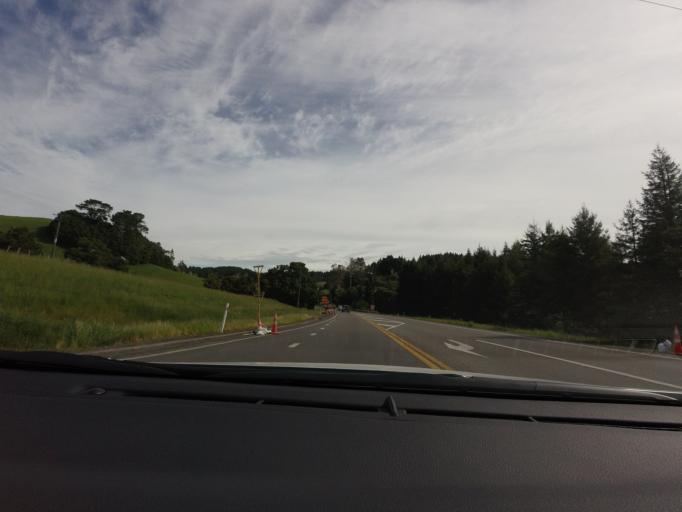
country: NZ
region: Auckland
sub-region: Auckland
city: Warkworth
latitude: -36.4905
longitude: 174.6593
